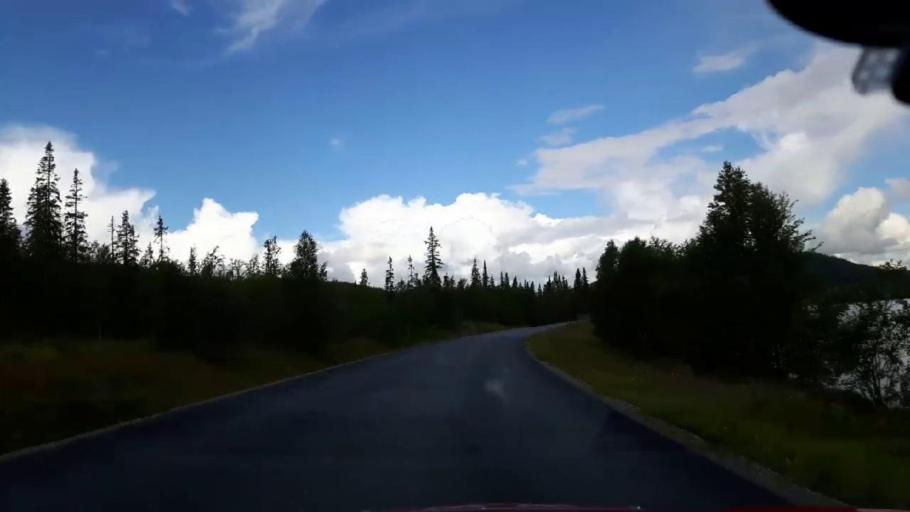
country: SE
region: Vaesterbotten
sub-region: Vilhelmina Kommun
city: Sjoberg
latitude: 65.0115
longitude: 15.1746
